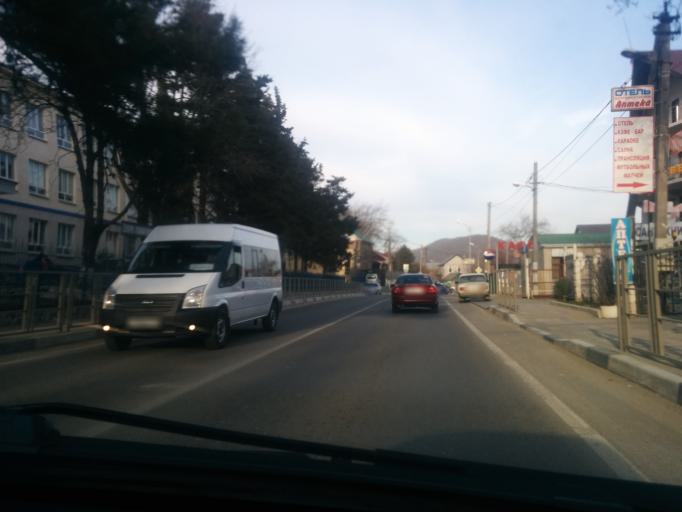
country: RU
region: Krasnodarskiy
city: Novomikhaylovskiy
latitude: 44.2546
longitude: 38.8483
